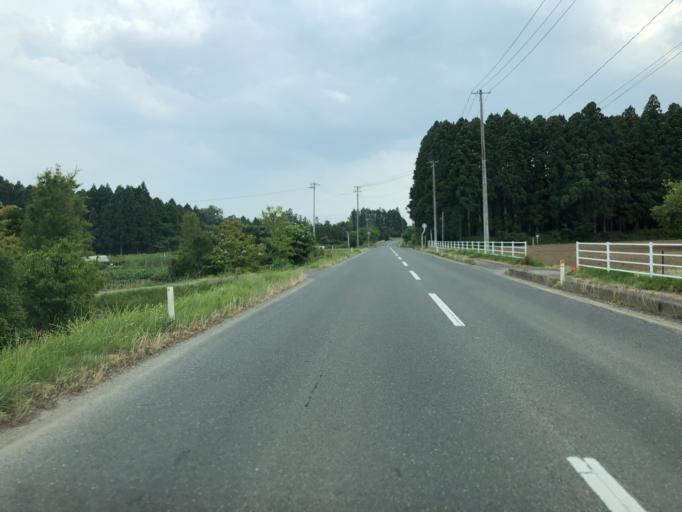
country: JP
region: Miyagi
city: Marumori
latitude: 37.8702
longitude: 140.8873
